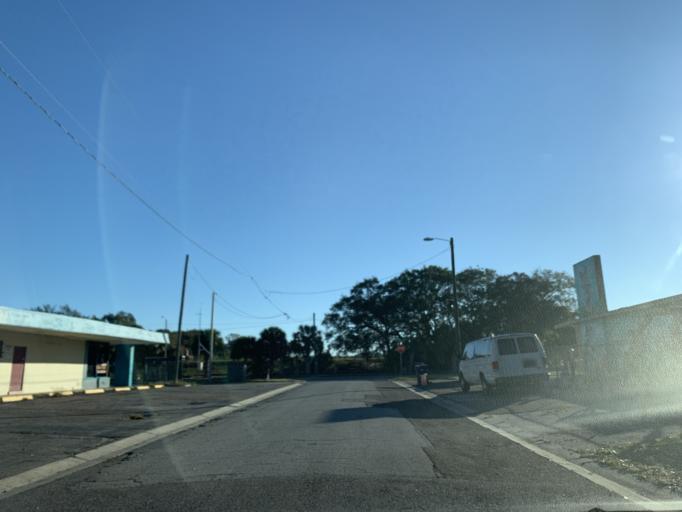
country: US
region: Florida
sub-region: Hillsborough County
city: University
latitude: 28.0411
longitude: -82.4269
